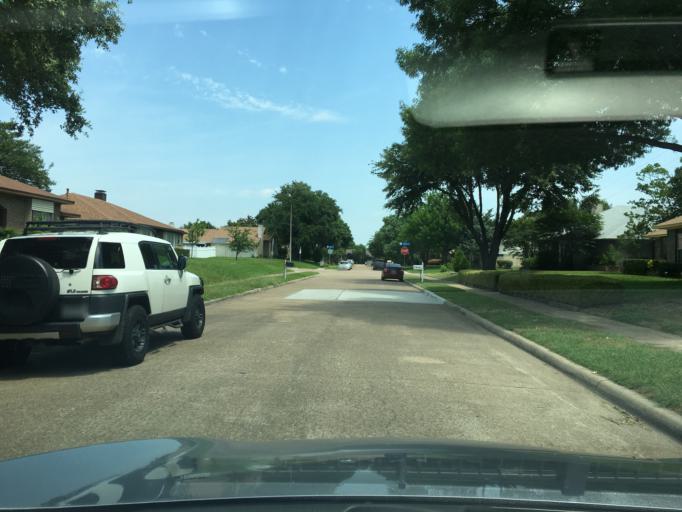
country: US
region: Texas
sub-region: Dallas County
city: Richardson
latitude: 32.9672
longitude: -96.6961
